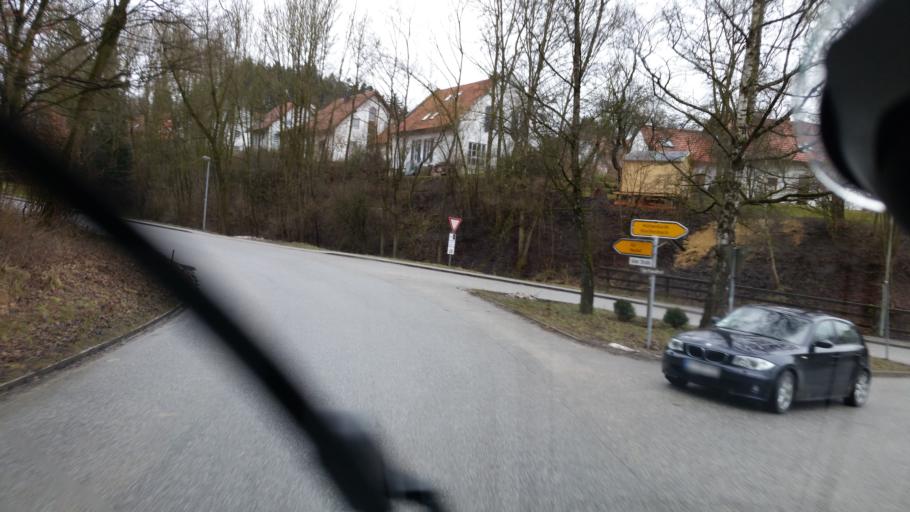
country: DE
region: Bavaria
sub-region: Lower Bavaria
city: Eching
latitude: 48.4957
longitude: 12.0653
